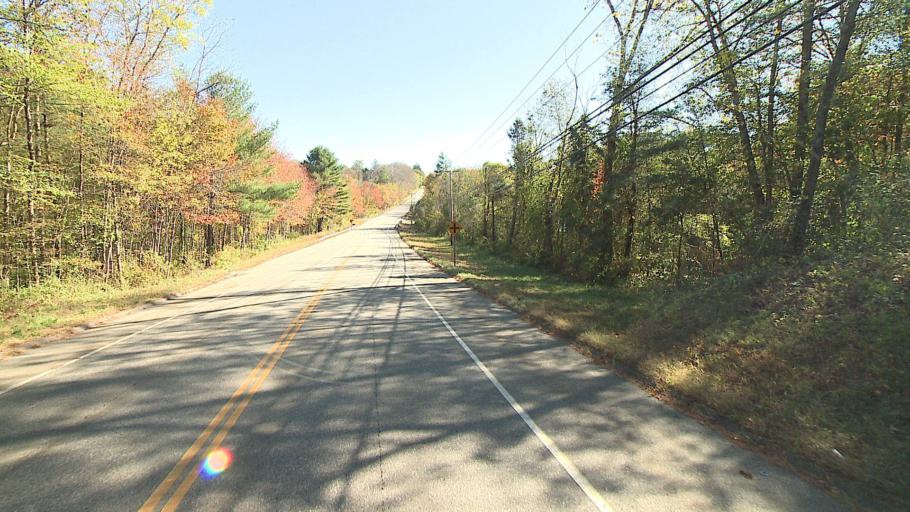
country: US
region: Connecticut
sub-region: Tolland County
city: Hebron
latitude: 41.6580
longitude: -72.3745
